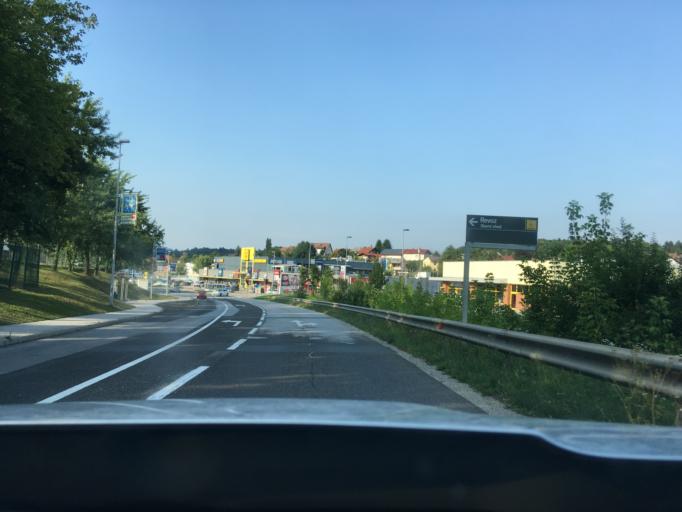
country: SI
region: Novo Mesto
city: Novo Mesto
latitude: 45.7949
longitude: 15.1803
